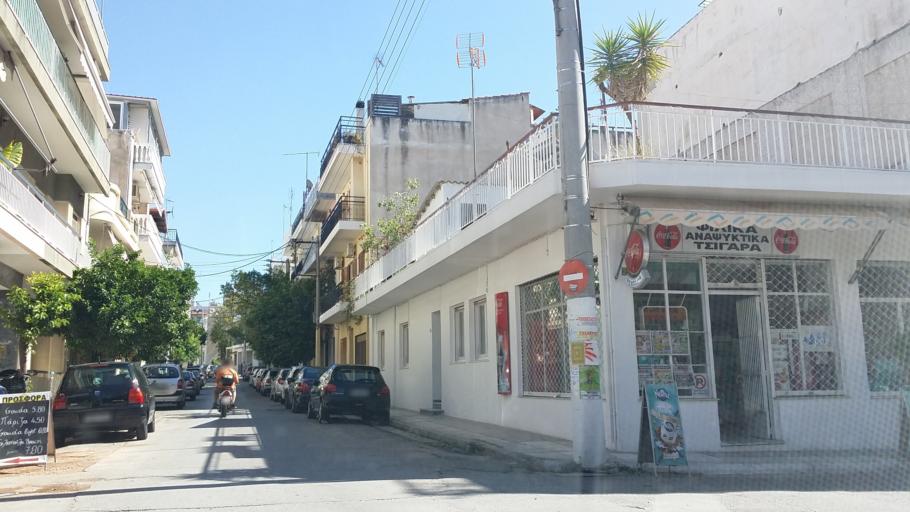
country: GR
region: Attica
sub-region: Nomarchia Athinas
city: Peristeri
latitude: 38.0188
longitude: 23.6997
